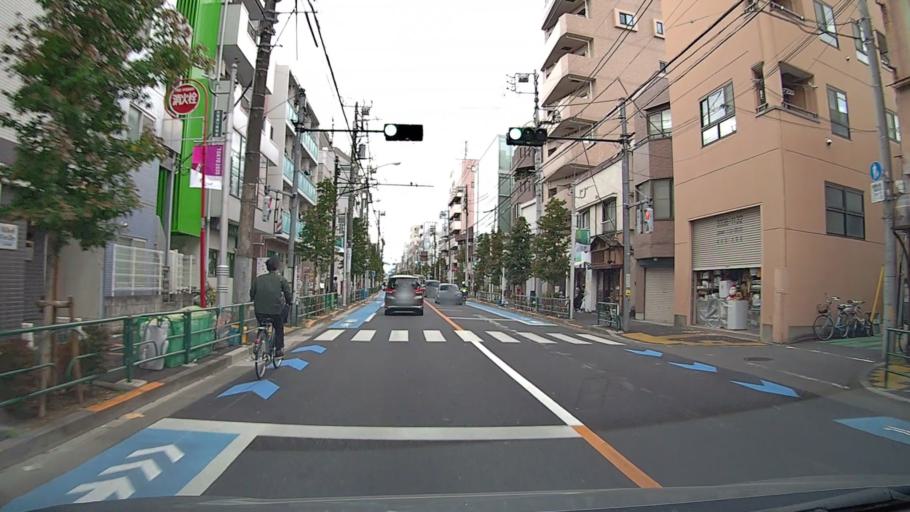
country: JP
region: Tokyo
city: Tokyo
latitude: 35.7103
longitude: 139.6477
